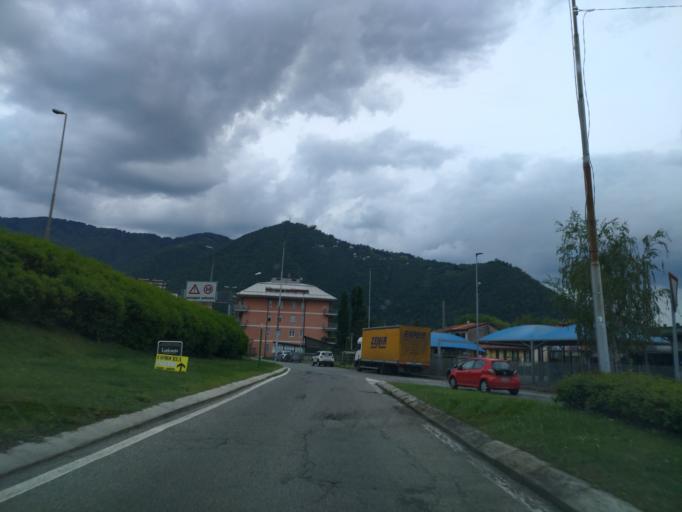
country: IT
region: Lombardy
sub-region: Provincia di Como
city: Cernobbio
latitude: 45.8361
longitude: 9.0676
